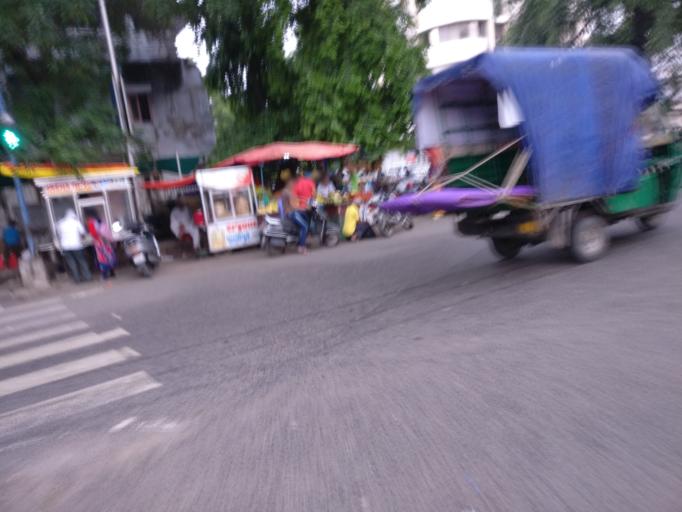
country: IN
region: Gujarat
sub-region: Ahmadabad
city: Ahmedabad
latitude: 23.0095
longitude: 72.5624
